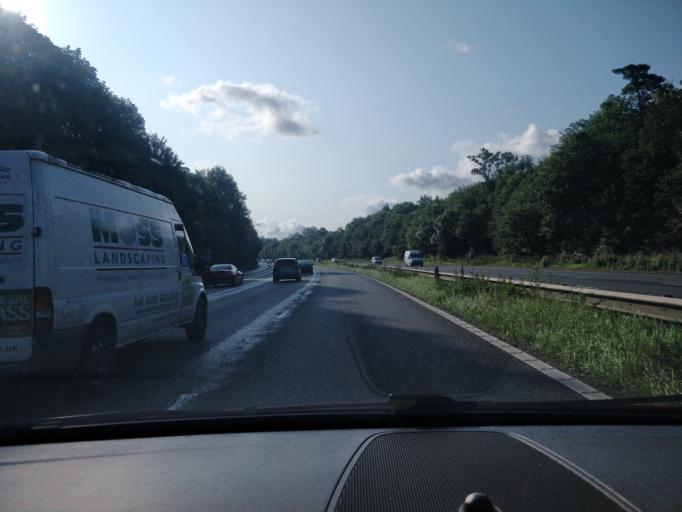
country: GB
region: England
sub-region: Knowsley
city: Huyton
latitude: 53.4320
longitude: -2.8488
